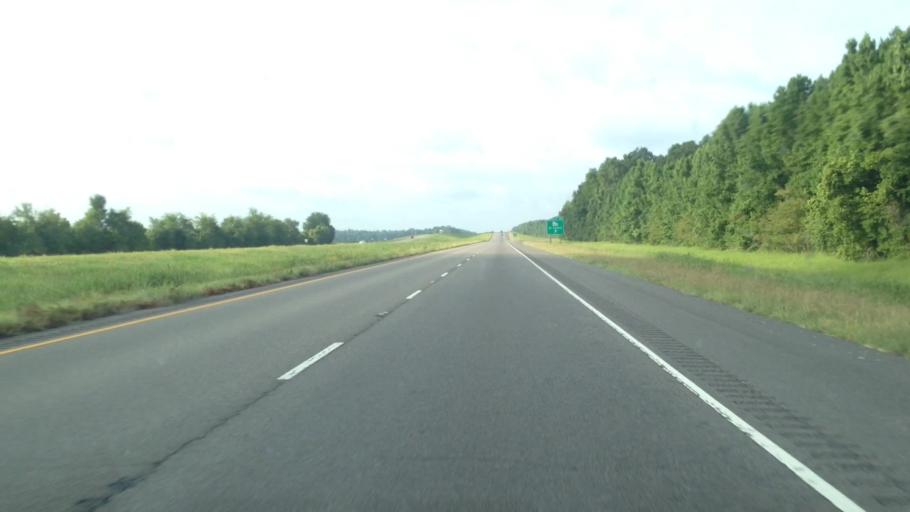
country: US
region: Louisiana
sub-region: Avoyelles Parish
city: Bunkie
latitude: 30.8738
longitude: -92.2279
